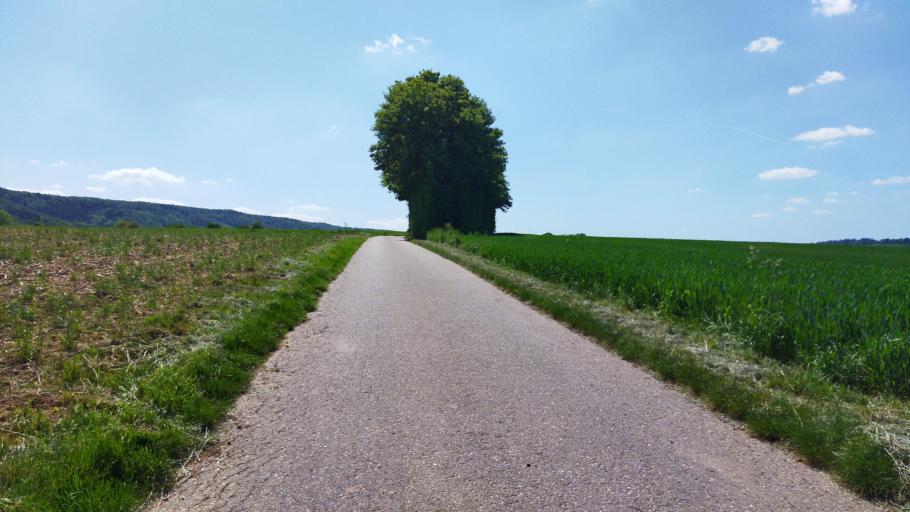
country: DE
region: Baden-Wuerttemberg
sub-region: Regierungsbezirk Stuttgart
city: Pfaffenhofen
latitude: 49.0570
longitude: 8.9867
